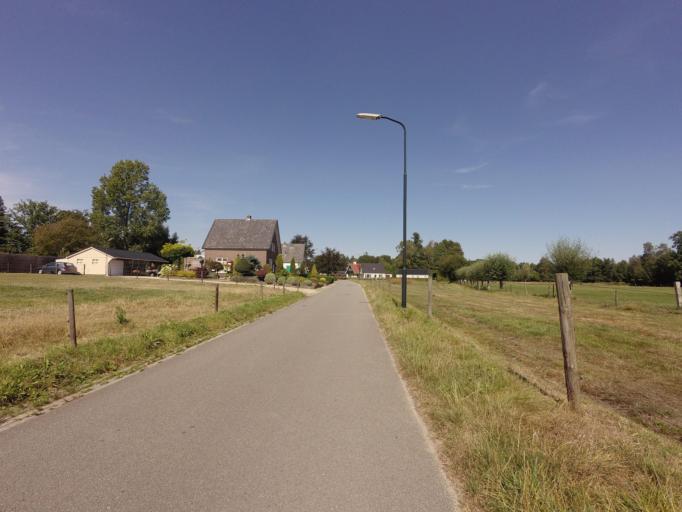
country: NL
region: Gelderland
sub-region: Gemeente Apeldoorn
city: Loenen
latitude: 52.1137
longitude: 6.0242
